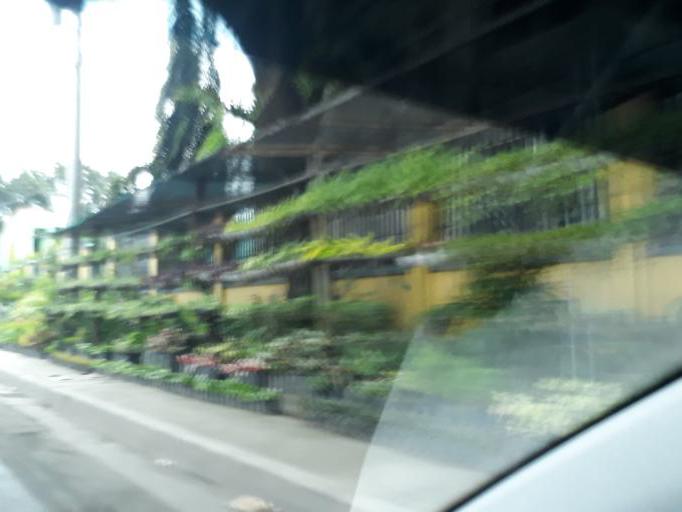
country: PH
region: Calabarzon
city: Del Monte
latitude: 14.6295
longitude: 120.9998
